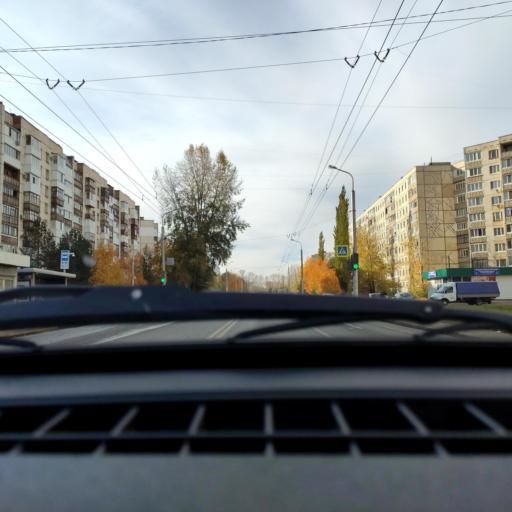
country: RU
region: Bashkortostan
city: Ufa
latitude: 54.7780
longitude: 56.1153
